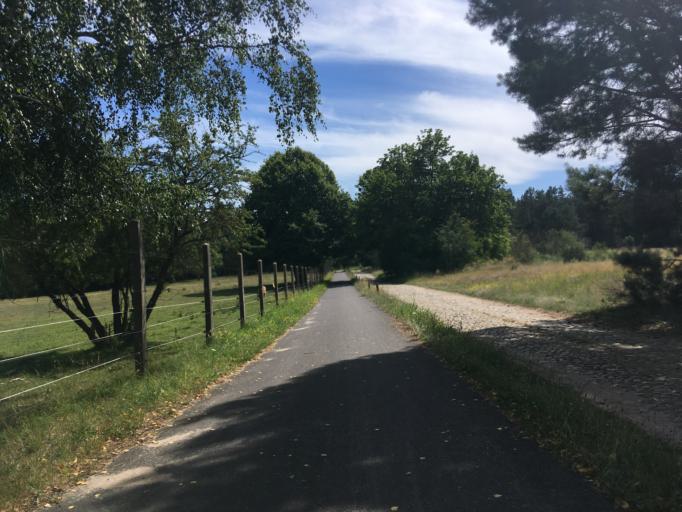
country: DE
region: Brandenburg
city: Rheinsberg
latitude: 53.0809
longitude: 12.9030
